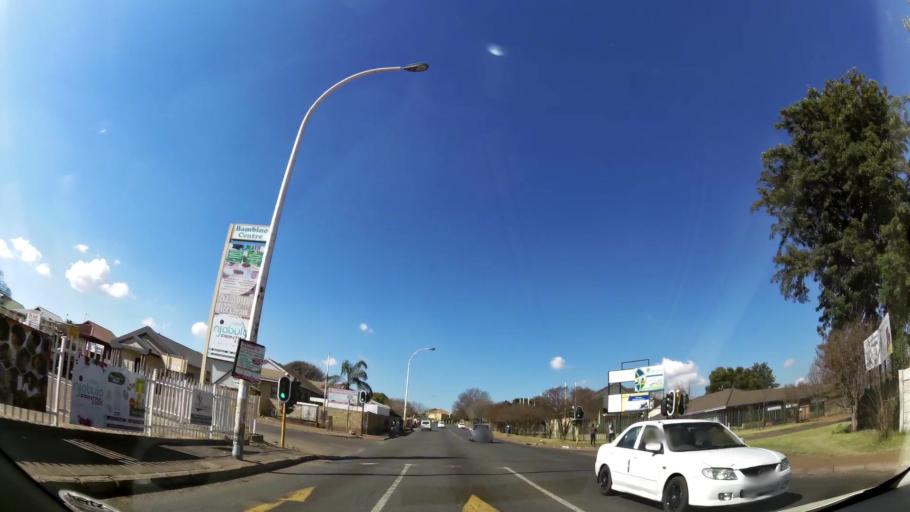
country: ZA
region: Mpumalanga
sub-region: Nkangala District Municipality
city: Witbank
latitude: -25.8787
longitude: 29.2166
